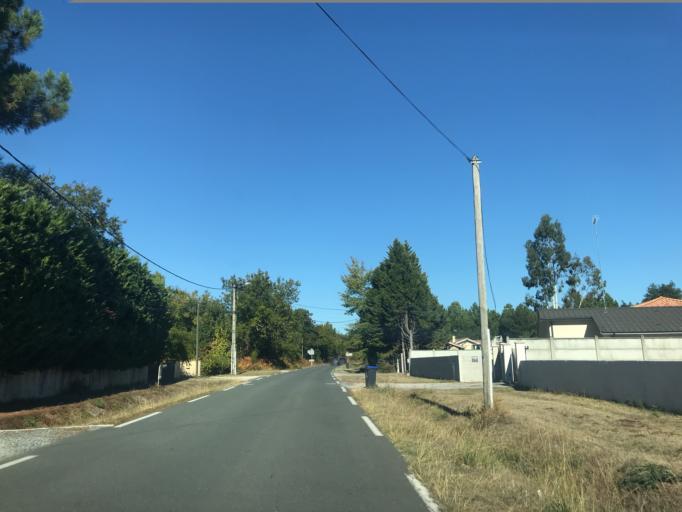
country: FR
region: Aquitaine
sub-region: Departement de la Gironde
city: Marcheprime
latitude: 44.6623
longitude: -0.8317
